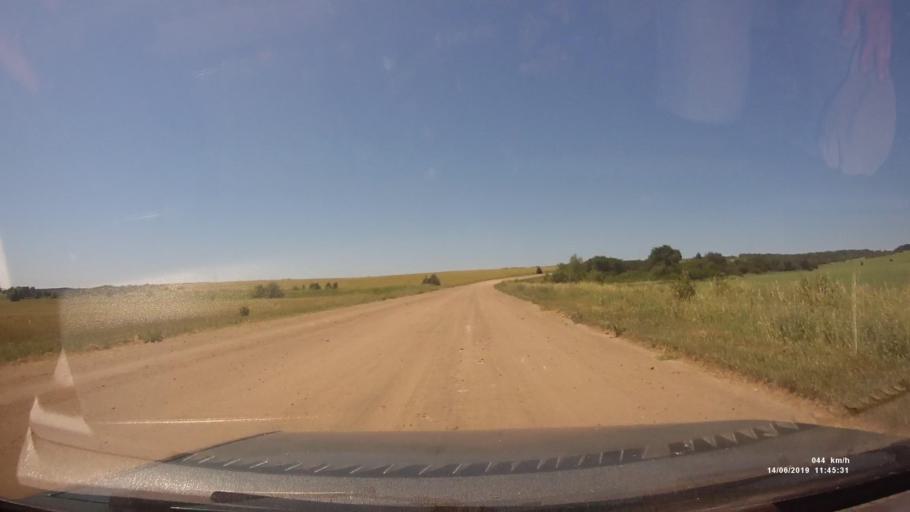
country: RU
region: Rostov
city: Kazanskaya
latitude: 49.8511
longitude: 41.3137
